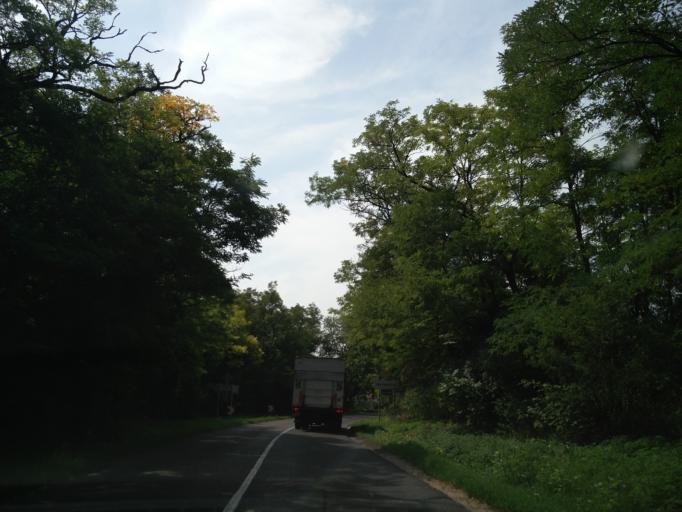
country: HU
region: Fejer
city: Lovasbereny
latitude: 47.3770
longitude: 18.5815
